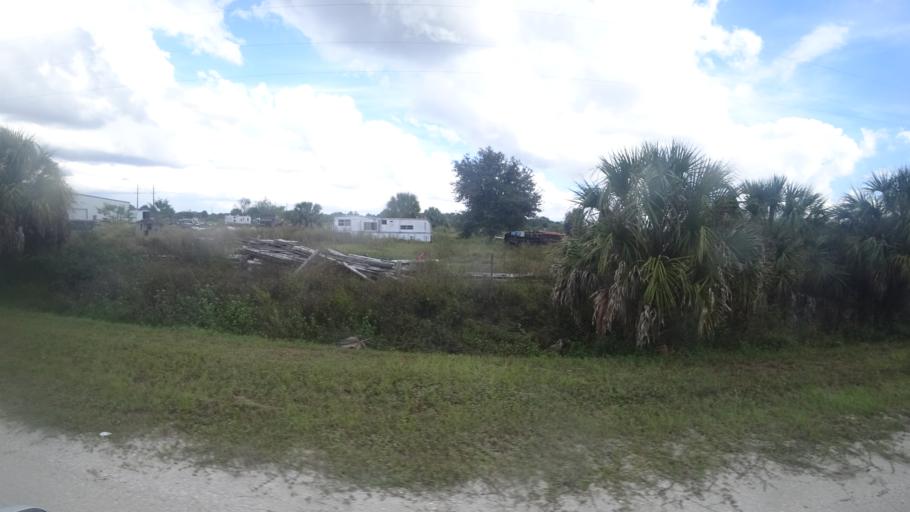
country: US
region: Florida
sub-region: Manatee County
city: Memphis
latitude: 27.6210
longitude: -82.5150
